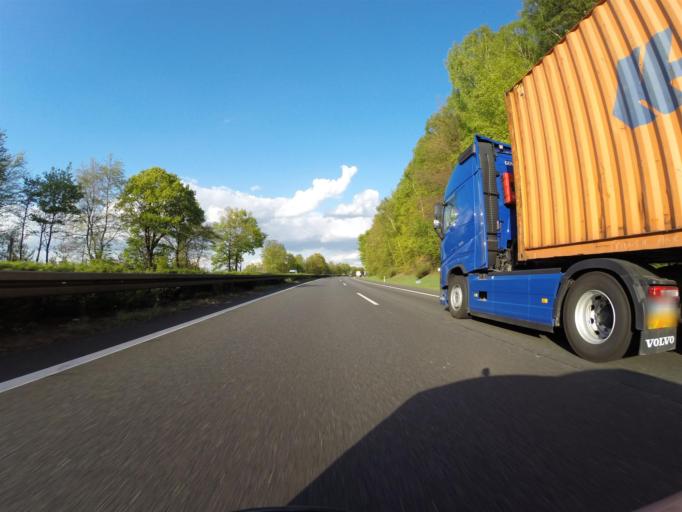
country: DE
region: Saarland
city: Sankt Ingbert
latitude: 49.2714
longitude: 7.1433
